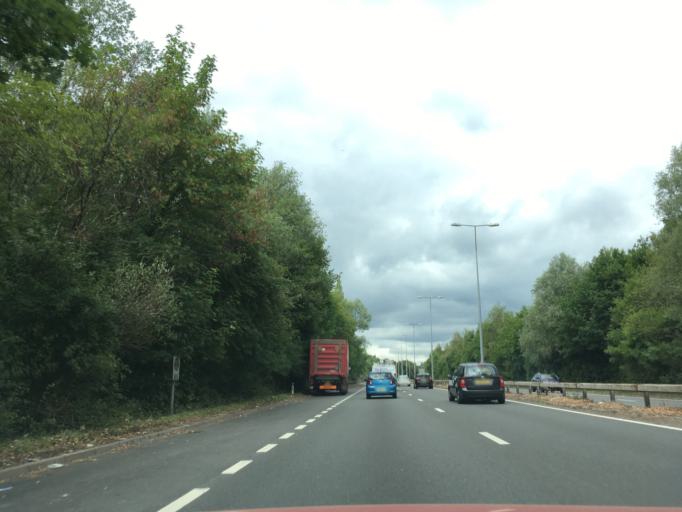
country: GB
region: Wales
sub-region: Torfaen County Borough
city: New Inn
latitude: 51.6838
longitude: -3.0182
